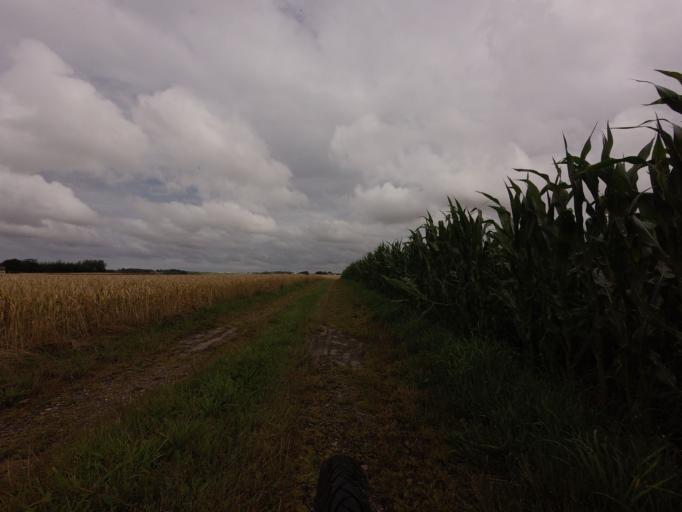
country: DK
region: North Denmark
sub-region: Jammerbugt Kommune
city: Pandrup
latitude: 57.2944
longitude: 9.7410
